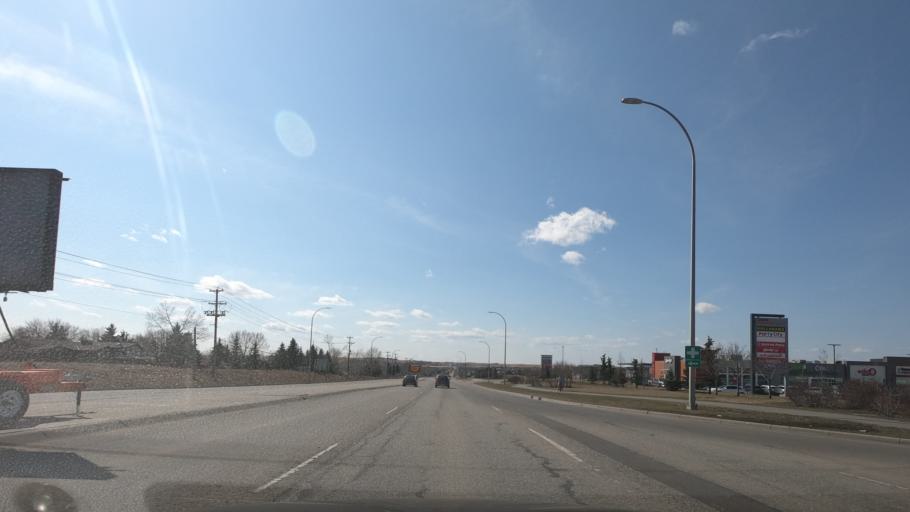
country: CA
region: Alberta
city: Airdrie
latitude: 51.3001
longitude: -114.0075
